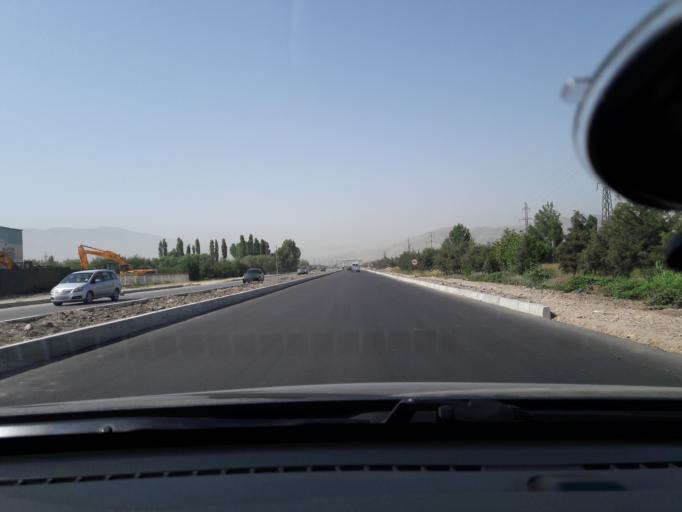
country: TJ
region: Dushanbe
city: Boshkengash
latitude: 38.4828
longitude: 68.7476
